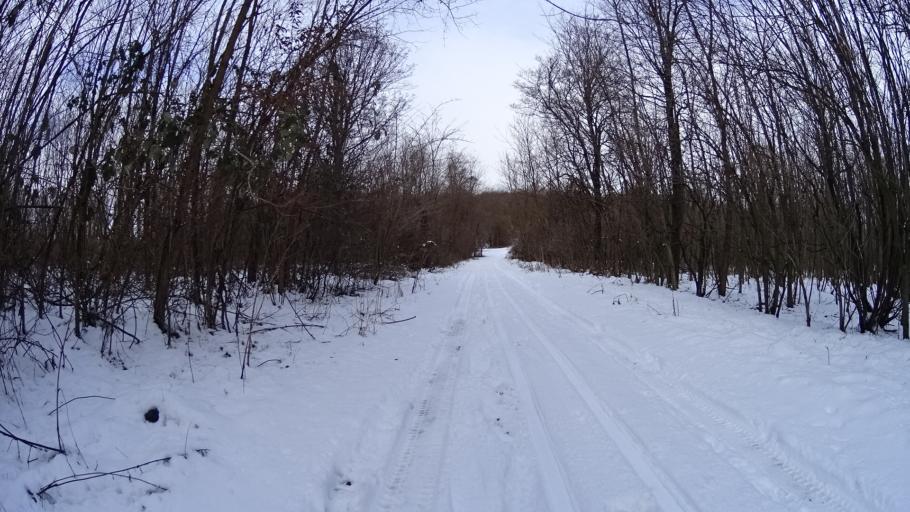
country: AT
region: Lower Austria
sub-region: Politischer Bezirk Korneuburg
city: Leobendorf
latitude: 48.4063
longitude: 16.3312
